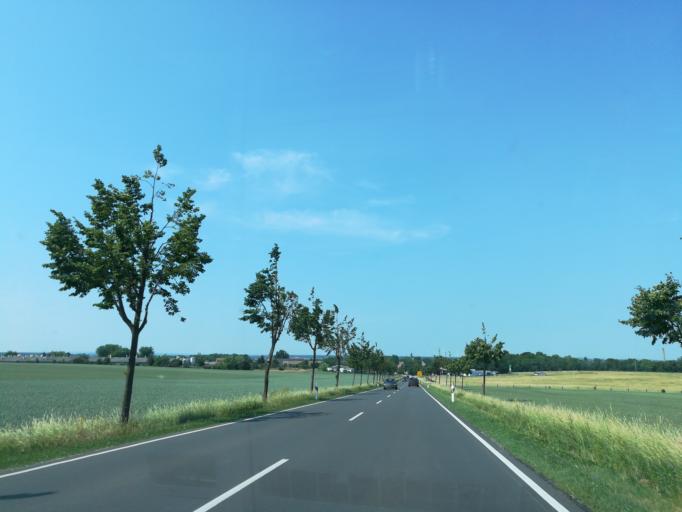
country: DE
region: Saxony-Anhalt
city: Schneidlingen
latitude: 51.8844
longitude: 11.4463
